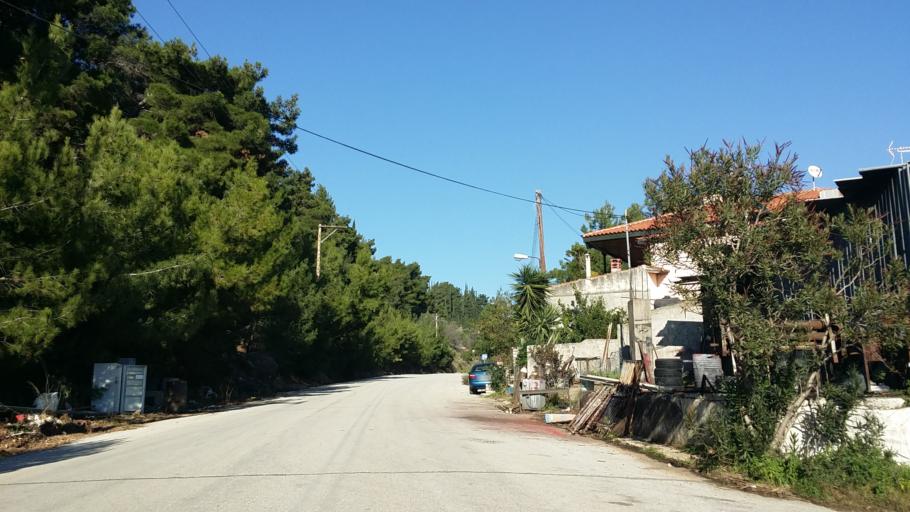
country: GR
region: West Greece
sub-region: Nomos Aitolias kai Akarnanias
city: Astakos
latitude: 38.5334
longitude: 21.0734
